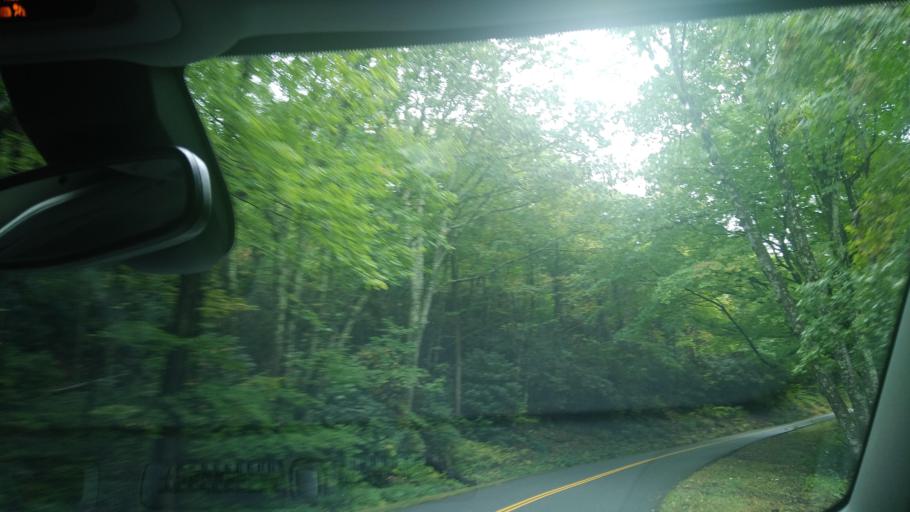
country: US
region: North Carolina
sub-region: Mitchell County
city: Spruce Pine
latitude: 35.9066
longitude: -81.9703
